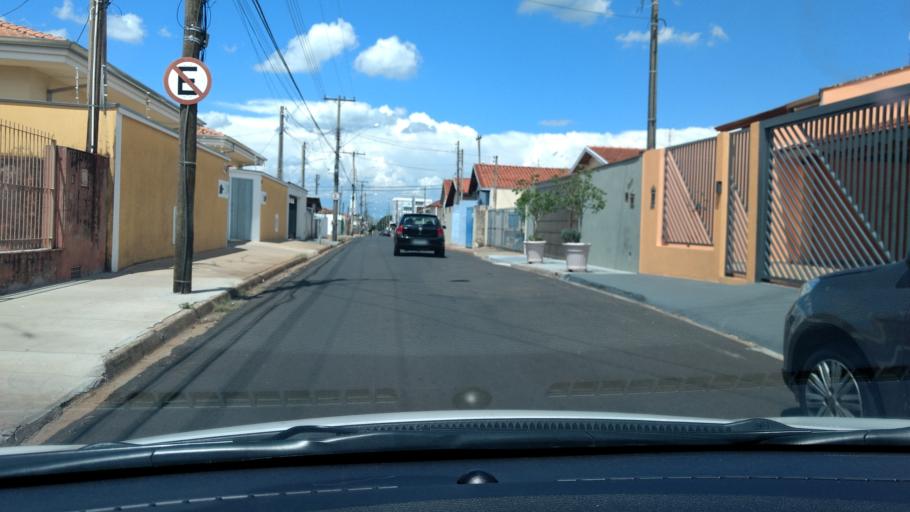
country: BR
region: Sao Paulo
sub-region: Botucatu
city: Botucatu
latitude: -22.8654
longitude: -48.4526
